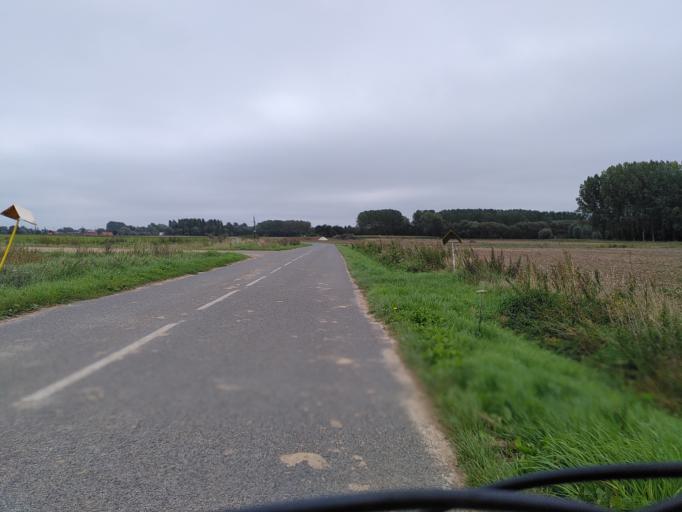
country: FR
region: Nord-Pas-de-Calais
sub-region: Departement du Pas-de-Calais
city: Aire-sur-la-Lys
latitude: 50.6479
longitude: 2.3712
